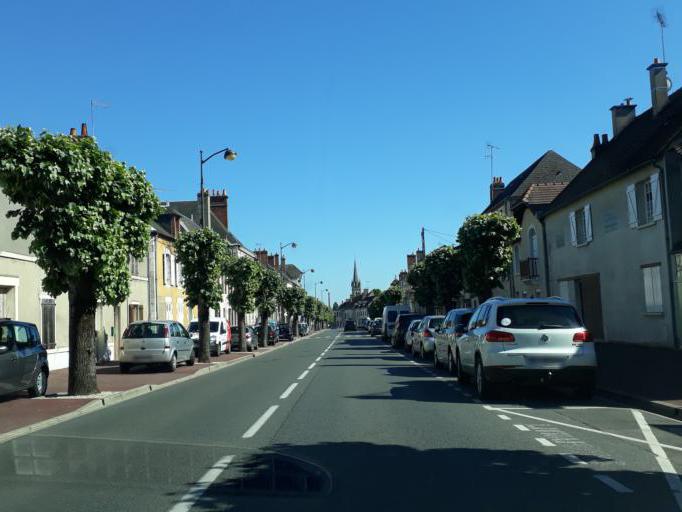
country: FR
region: Centre
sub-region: Departement du Loiret
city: Briare
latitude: 47.6428
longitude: 2.7350
